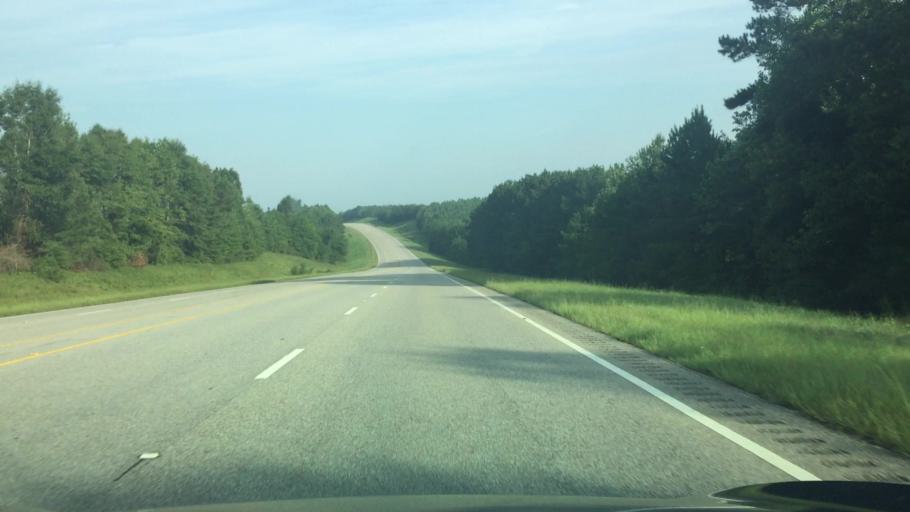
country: US
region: Alabama
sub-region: Butler County
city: Georgiana
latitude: 31.4568
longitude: -86.6363
